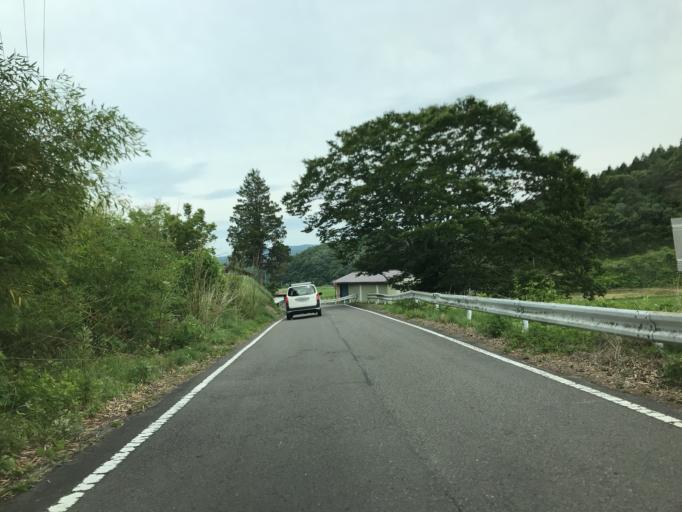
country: JP
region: Fukushima
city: Funehikimachi-funehiki
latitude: 37.4313
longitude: 140.7777
